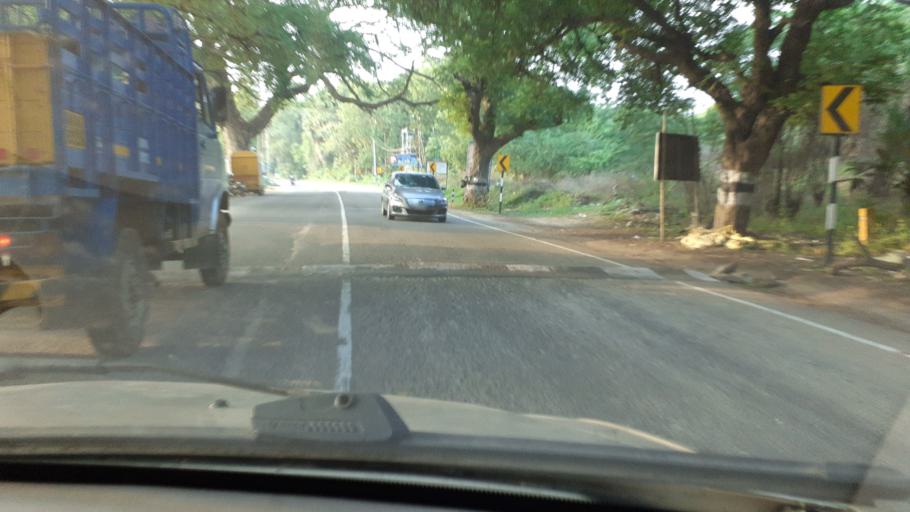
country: IN
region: Tamil Nadu
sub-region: Thoothukkudi
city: Srivaikuntam
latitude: 8.6294
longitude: 77.9059
